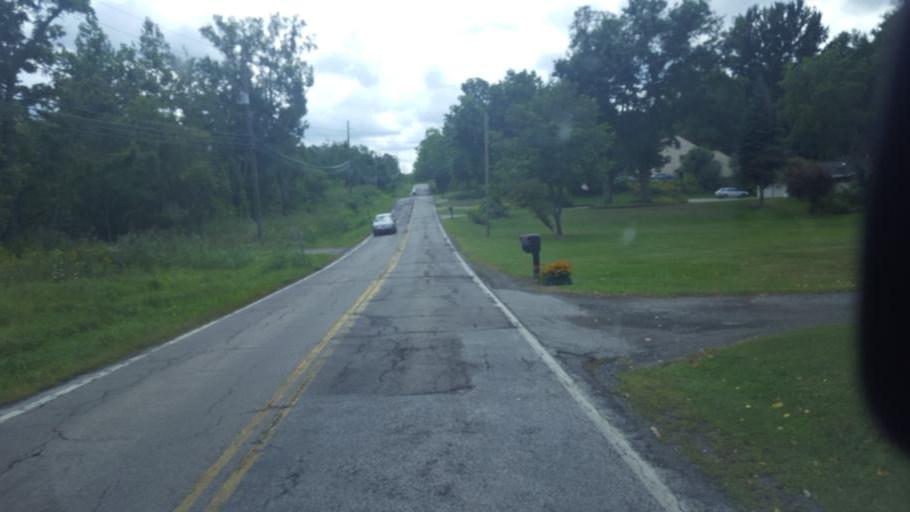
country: US
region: Ohio
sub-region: Lake County
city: Perry
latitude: 41.7185
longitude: -81.1797
